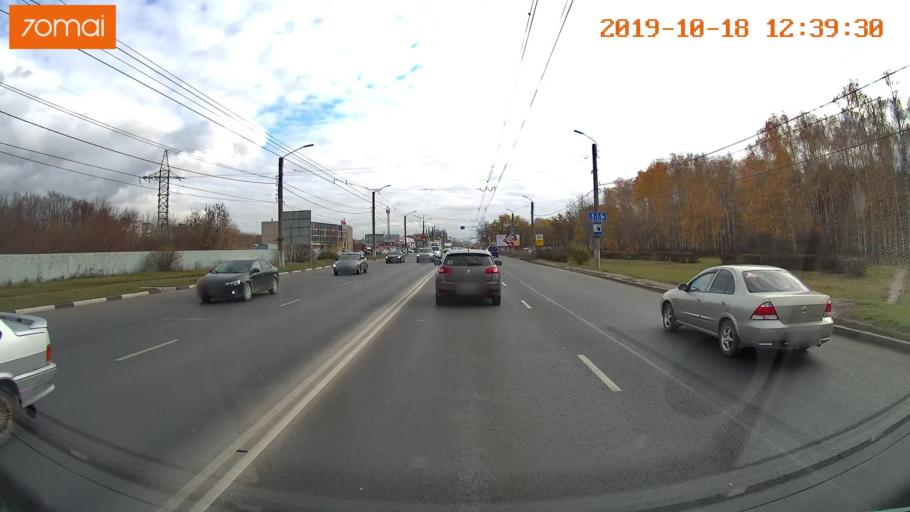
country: RU
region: Rjazan
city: Ryazan'
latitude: 54.6500
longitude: 39.6452
